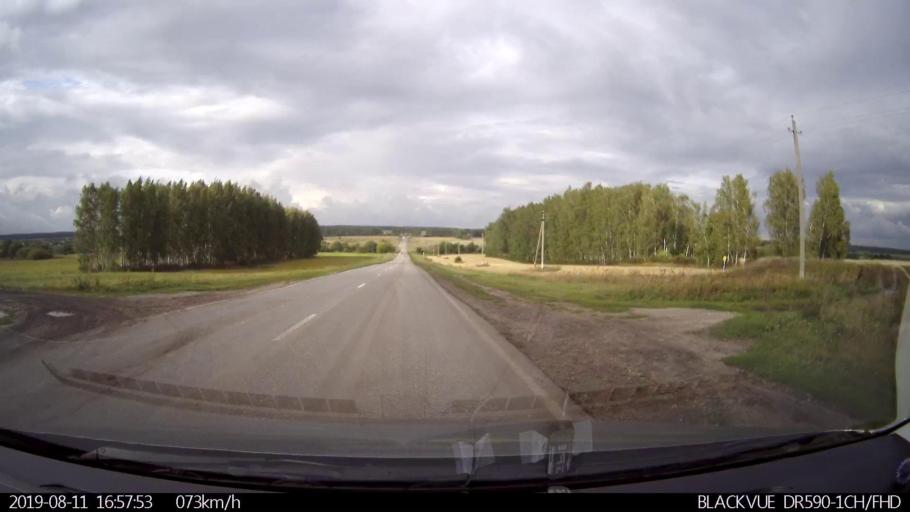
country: RU
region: Ulyanovsk
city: Mayna
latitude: 54.3024
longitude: 47.6547
